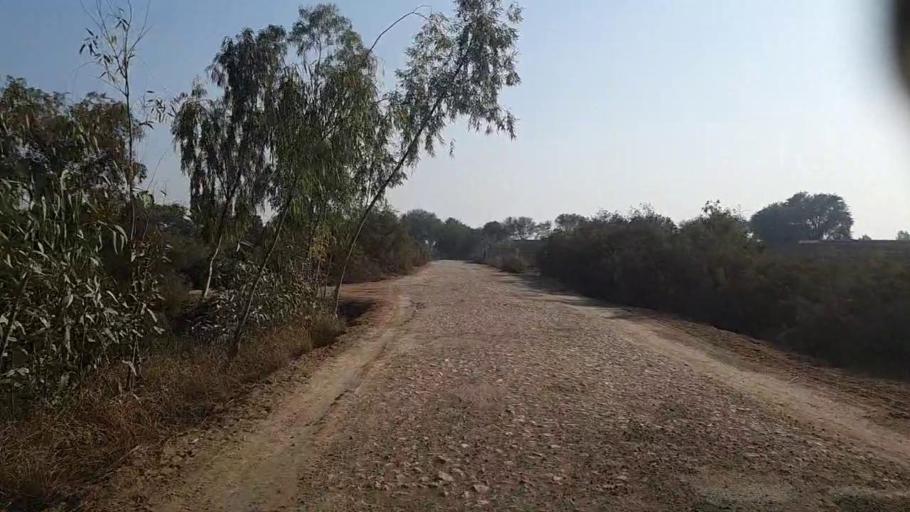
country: PK
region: Sindh
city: Mirpur Mathelo
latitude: 27.8848
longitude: 69.6111
